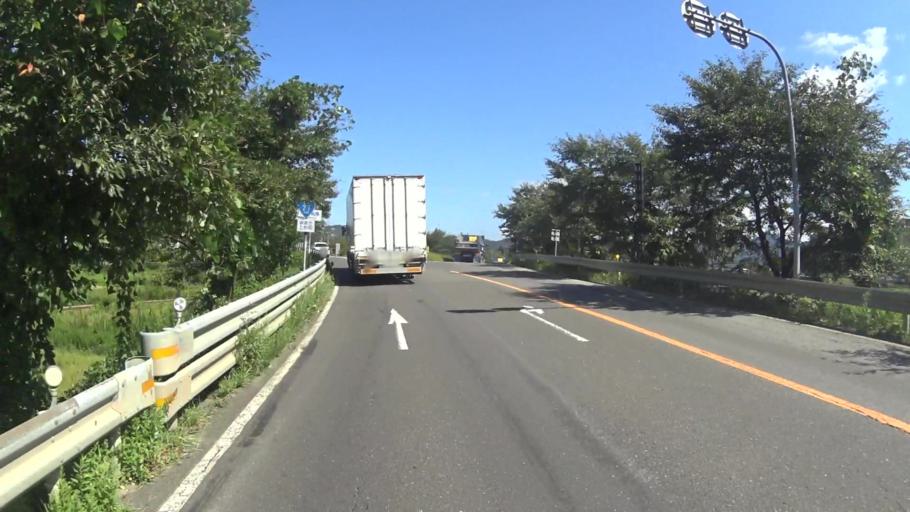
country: JP
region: Kyoto
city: Ayabe
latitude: 35.3591
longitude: 135.3162
